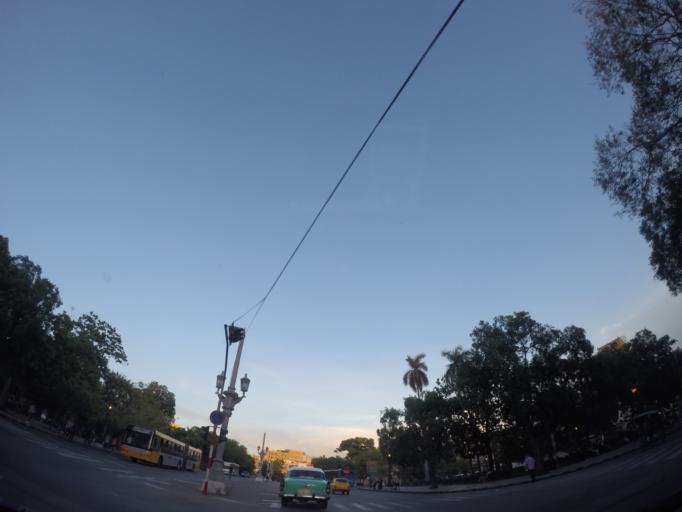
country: CU
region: La Habana
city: Centro Habana
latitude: 23.1325
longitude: -82.3607
